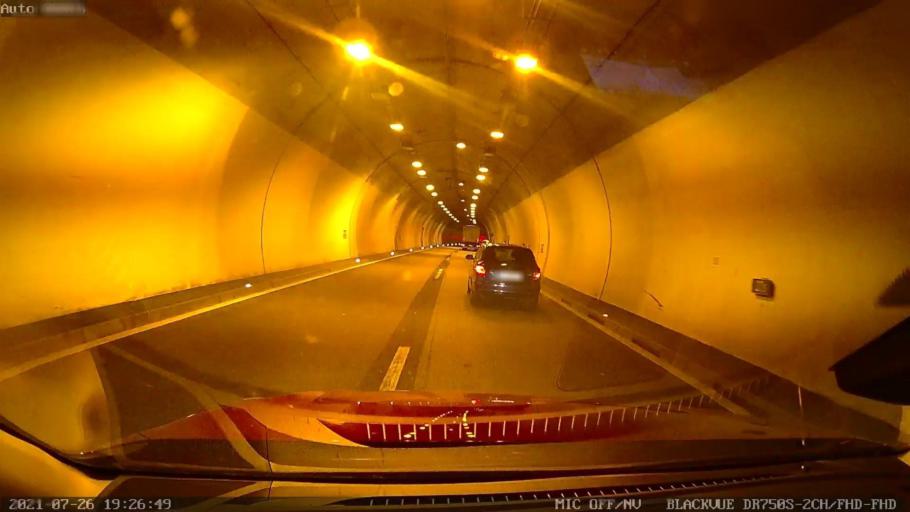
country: AT
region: Upper Austria
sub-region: Politischer Bezirk Kirchdorf an der Krems
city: Micheldorf in Oberoesterreich
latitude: 47.8488
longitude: 14.1654
